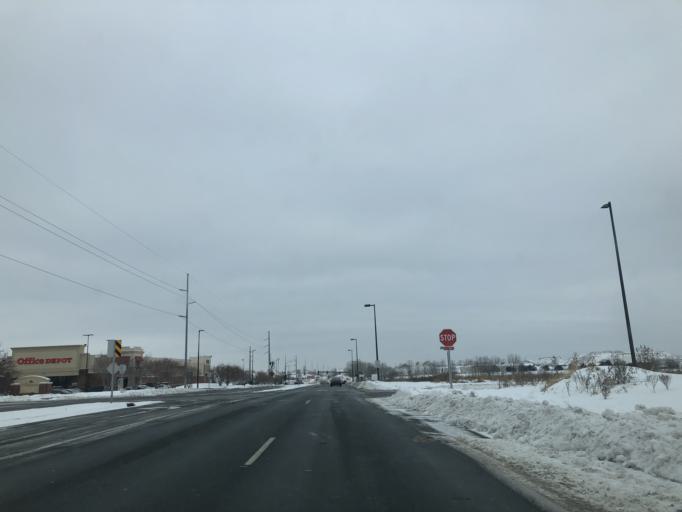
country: US
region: Minnesota
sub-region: Hennepin County
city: Osseo
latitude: 45.0916
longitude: -93.4214
